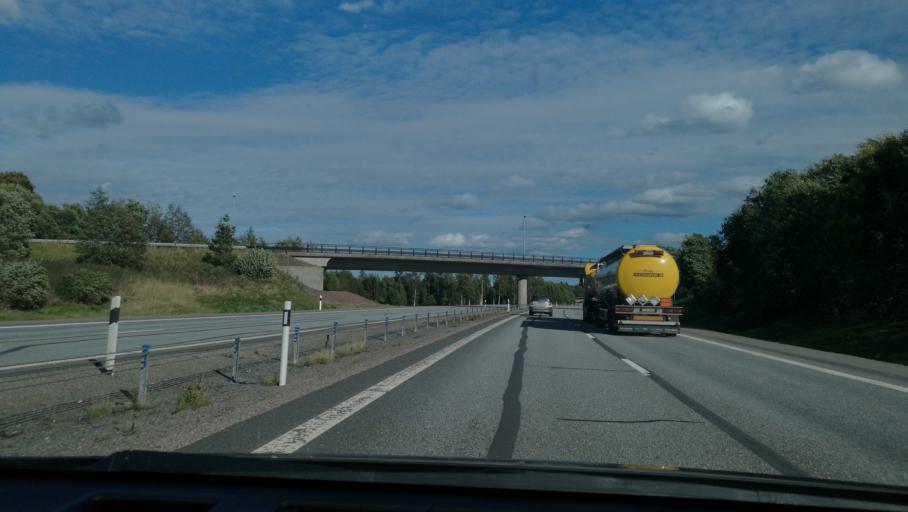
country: SE
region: OErebro
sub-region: Lekebergs Kommun
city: Fjugesta
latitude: 59.0346
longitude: 14.8550
